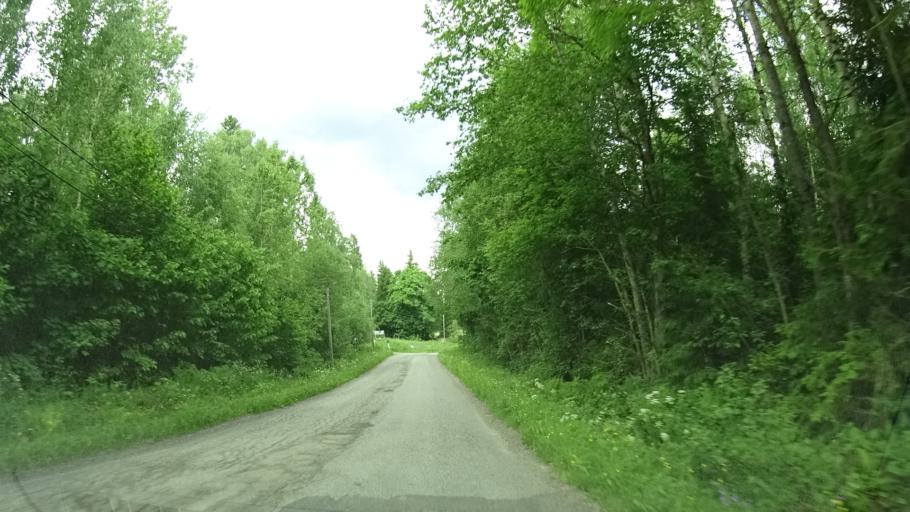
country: FI
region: Uusimaa
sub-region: Helsinki
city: Siuntio
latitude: 60.2114
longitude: 24.2377
